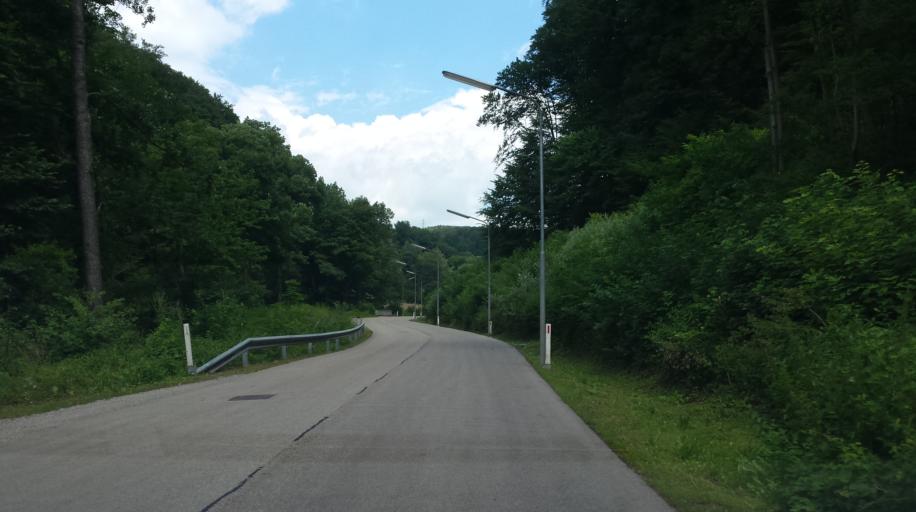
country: AT
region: Lower Austria
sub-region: Politischer Bezirk Wien-Umgebung
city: Mauerbach
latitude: 48.2382
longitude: 16.2043
